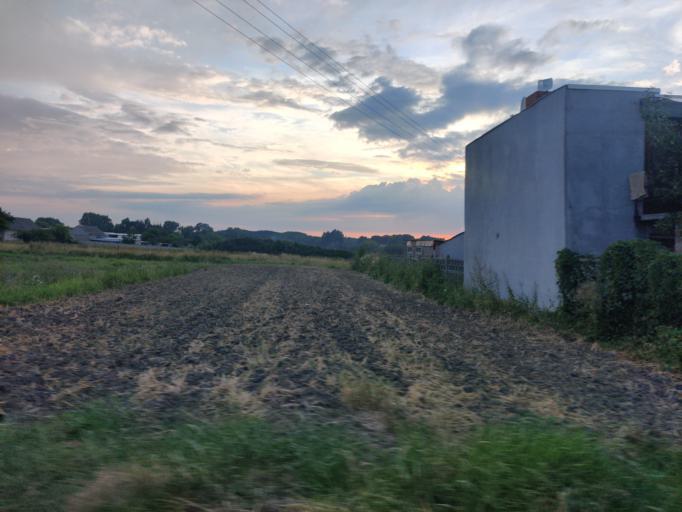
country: PL
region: Greater Poland Voivodeship
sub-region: Konin
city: Konin
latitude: 52.1936
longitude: 18.3140
